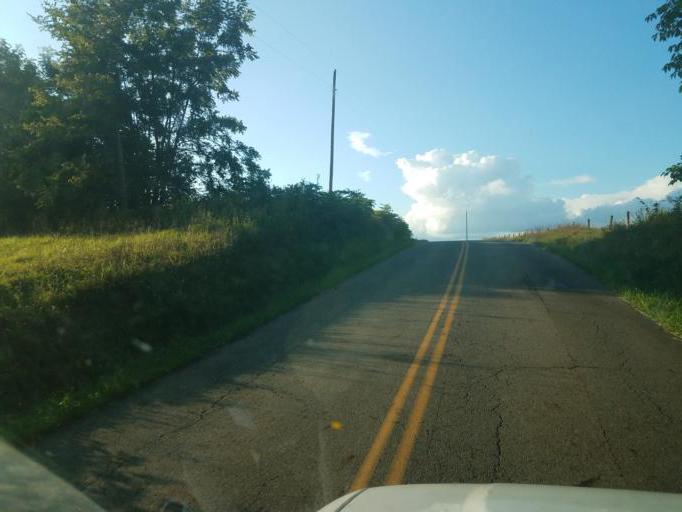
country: US
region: Ohio
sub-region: Knox County
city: Fredericktown
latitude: 40.4271
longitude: -82.6354
